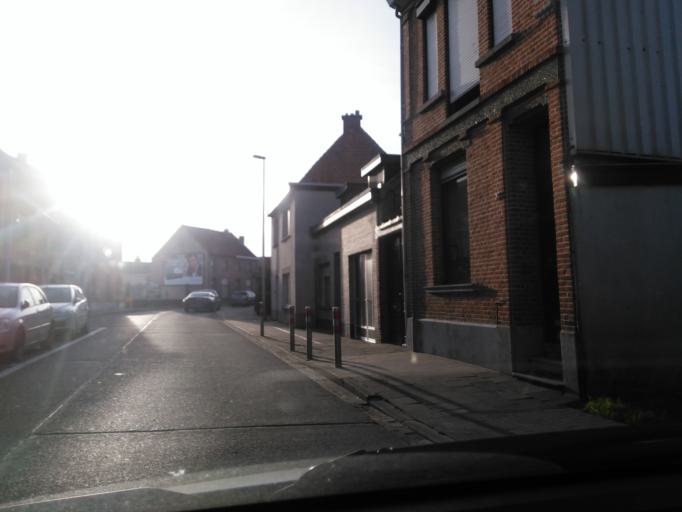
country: BE
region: Flanders
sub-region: Provincie Oost-Vlaanderen
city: Beveren
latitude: 51.2229
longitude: 4.2549
